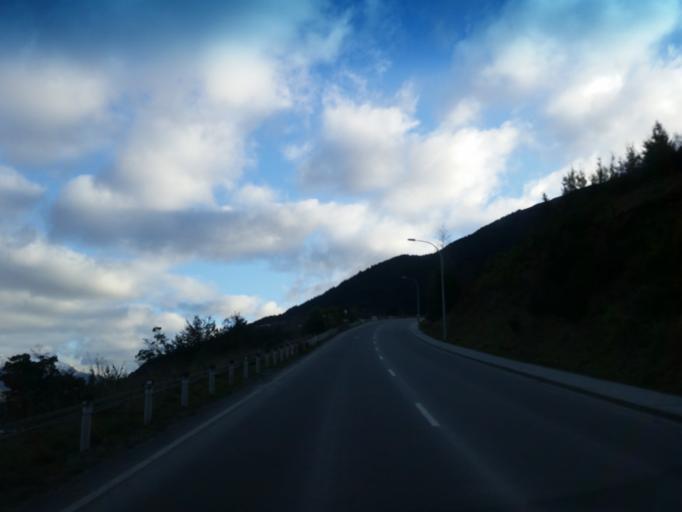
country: NZ
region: Otago
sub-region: Queenstown-Lakes District
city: Queenstown
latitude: -45.0380
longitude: 168.6464
